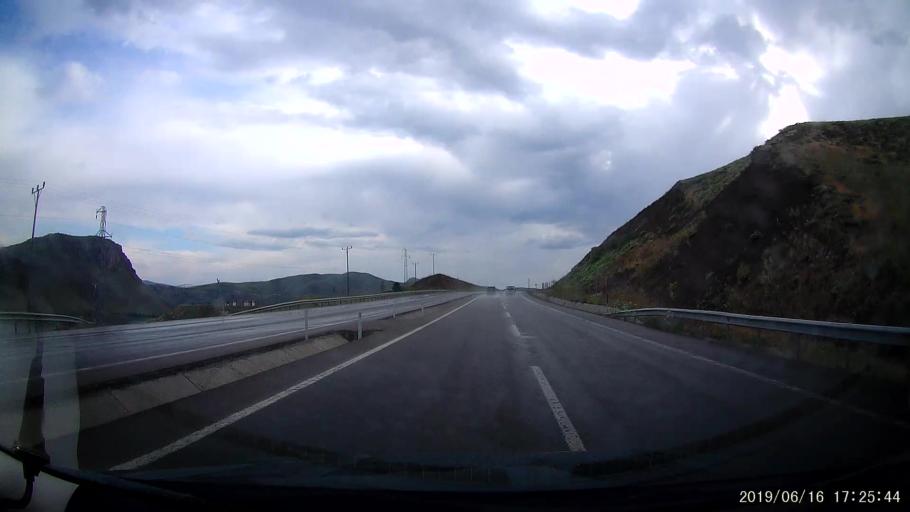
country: TR
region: Erzincan
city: Tercan
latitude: 39.7682
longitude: 40.4280
